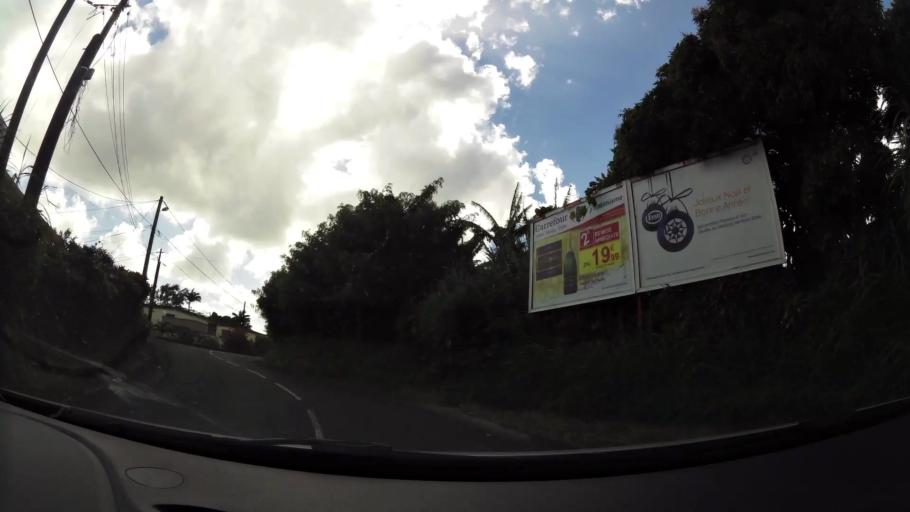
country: MQ
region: Martinique
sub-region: Martinique
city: Saint-Joseph
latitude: 14.6401
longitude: -61.0545
